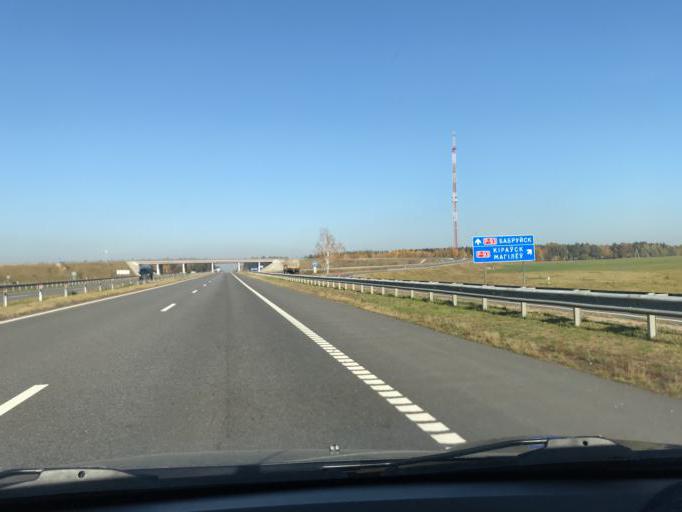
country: BY
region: Mogilev
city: Babruysk
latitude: 53.1818
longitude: 29.3577
